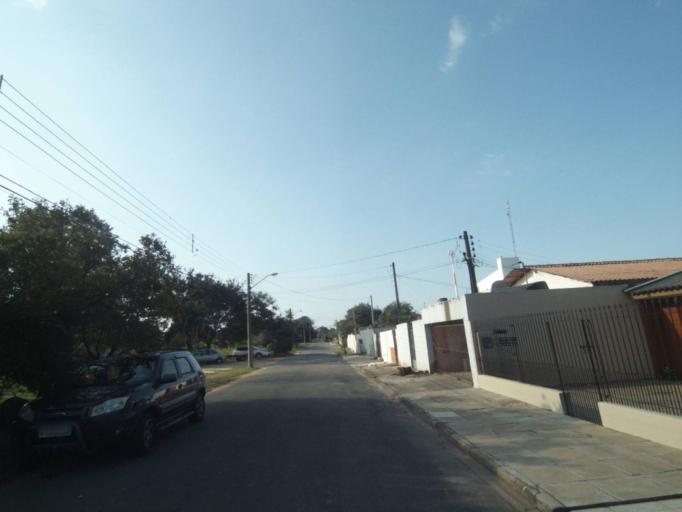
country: BR
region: Parana
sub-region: Curitiba
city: Curitiba
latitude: -25.4936
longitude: -49.3359
